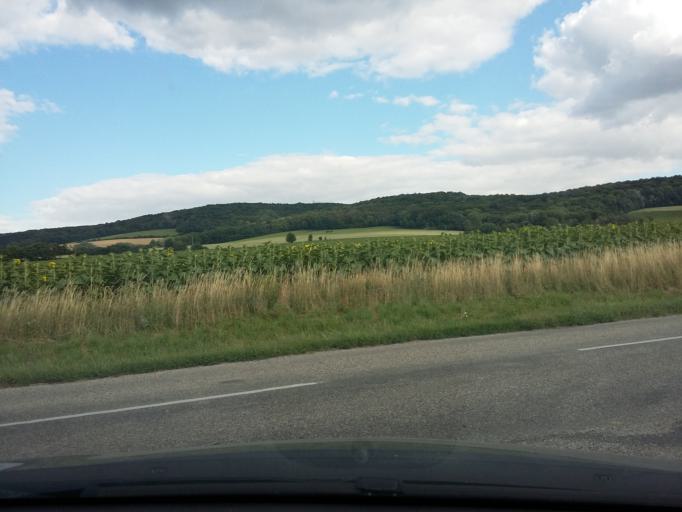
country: SK
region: Trnavsky
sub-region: Okres Senica
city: Senica
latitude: 48.5807
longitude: 17.3525
